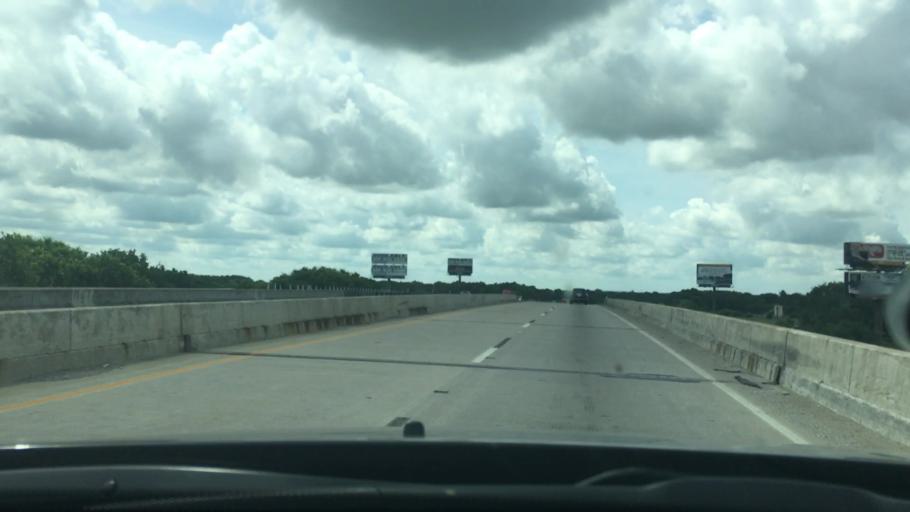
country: US
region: Oklahoma
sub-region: Love County
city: Marietta
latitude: 33.8357
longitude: -97.1320
